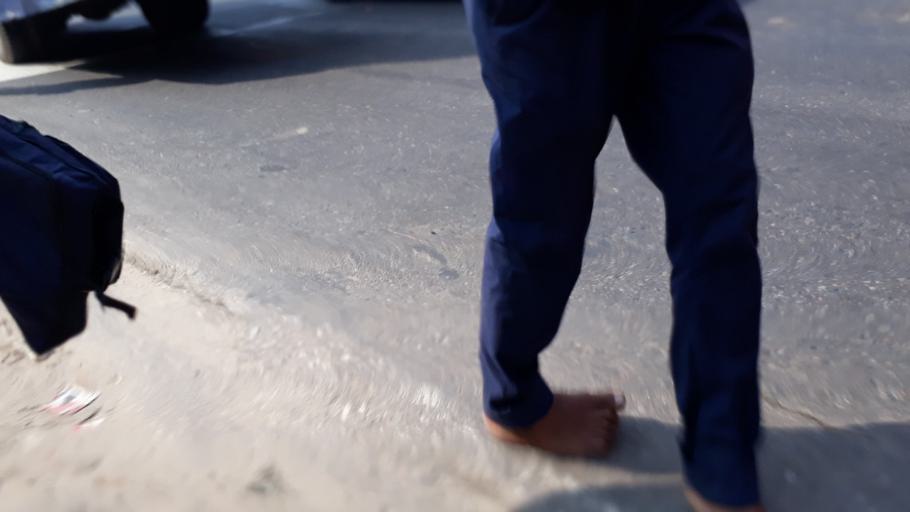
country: BD
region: Dhaka
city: Tungi
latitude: 23.8593
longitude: 90.2629
